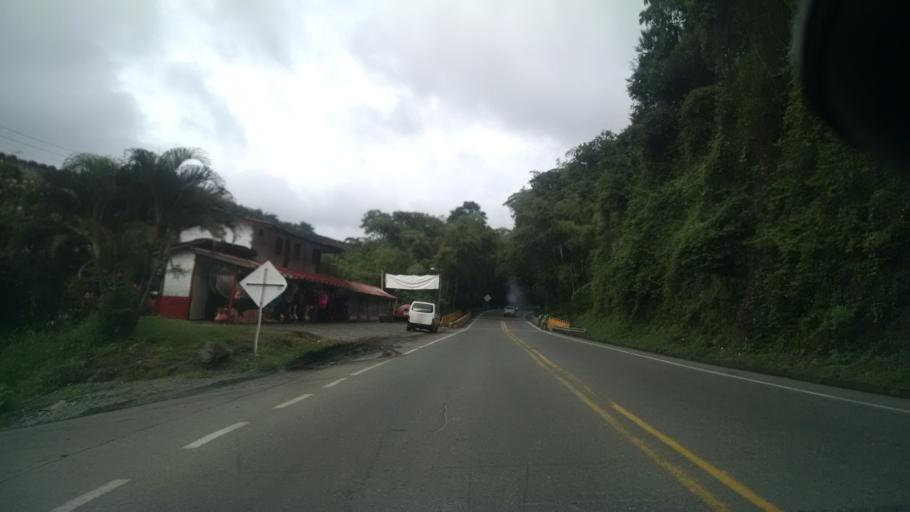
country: CO
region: Caldas
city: Palestina
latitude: 5.0702
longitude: -75.6221
